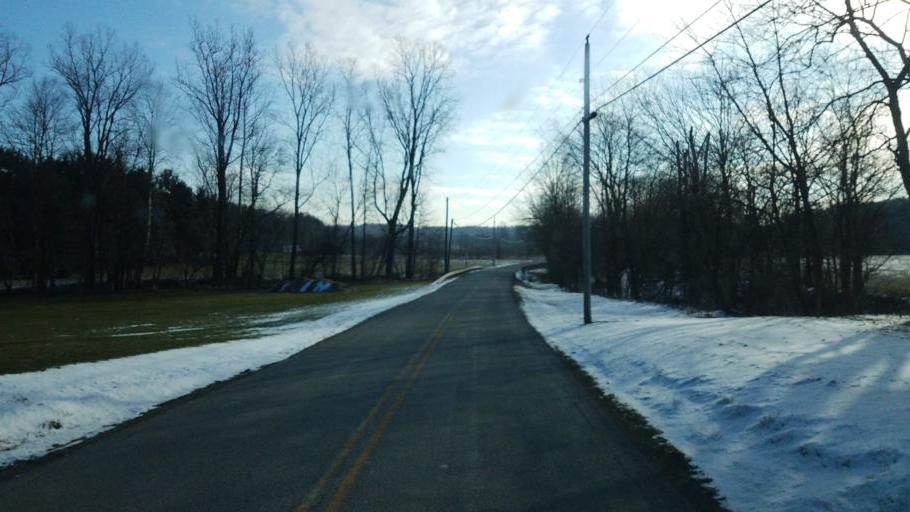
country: US
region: Ohio
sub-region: Sandusky County
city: Bellville
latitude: 40.6233
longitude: -82.5567
